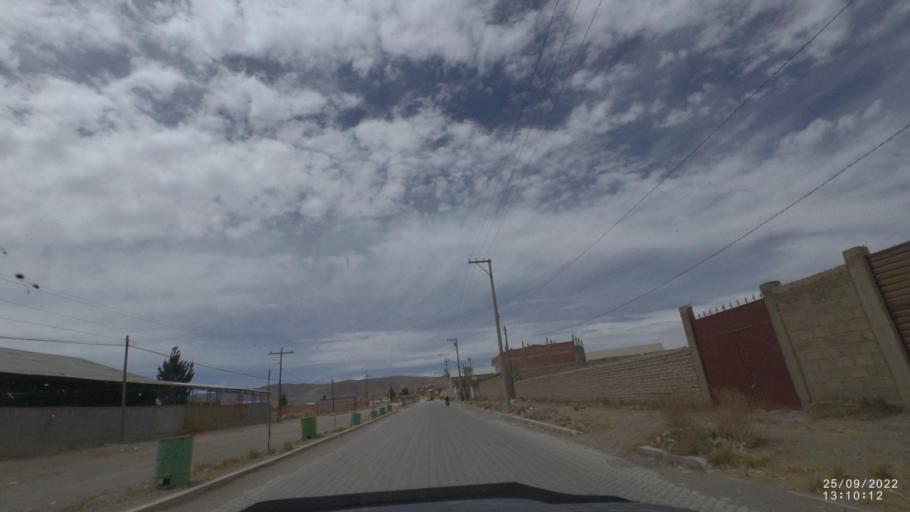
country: BO
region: Oruro
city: Oruro
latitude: -17.9723
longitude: -67.0506
